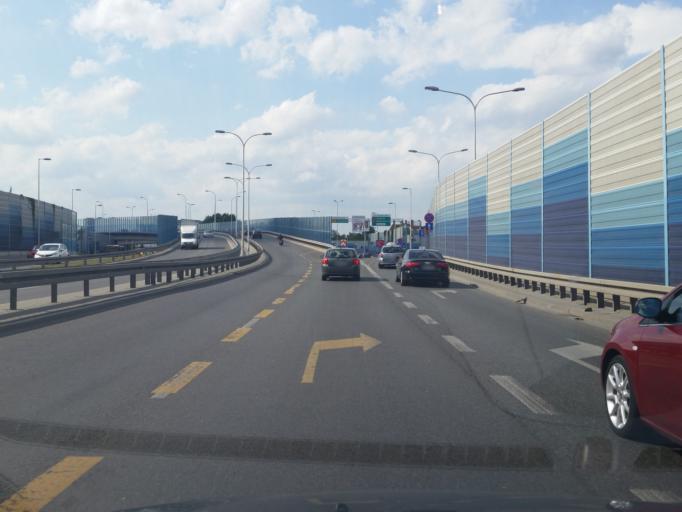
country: PL
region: Masovian Voivodeship
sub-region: Warszawa
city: Wlochy
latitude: 52.1954
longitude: 20.9321
